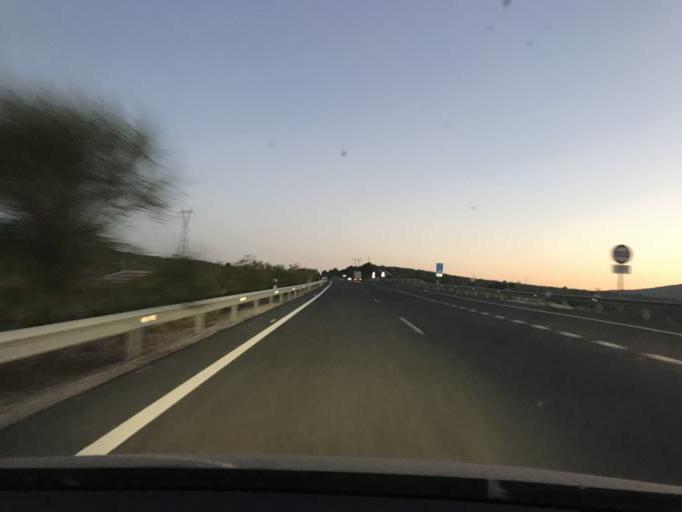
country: ES
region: Andalusia
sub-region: Province of Cordoba
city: Lucena
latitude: 37.4055
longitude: -4.5306
